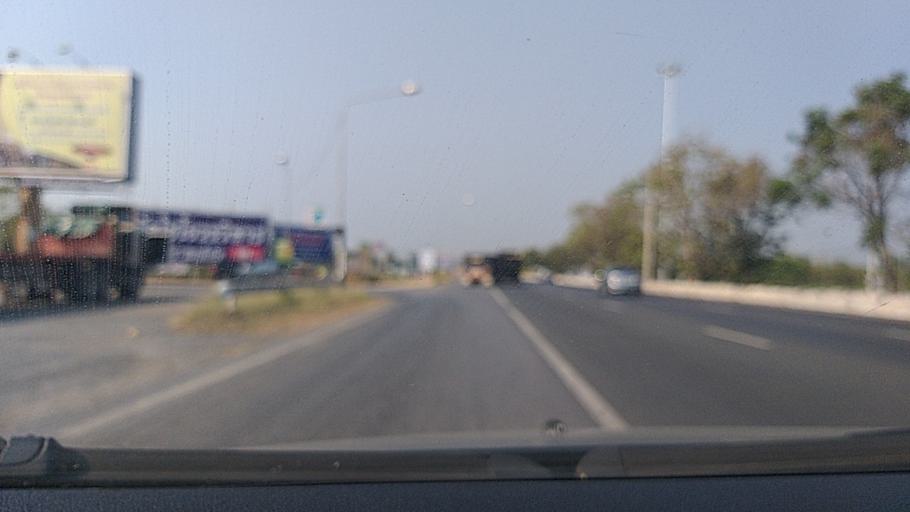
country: TH
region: Ang Thong
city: Chaiyo
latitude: 14.7234
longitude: 100.4551
